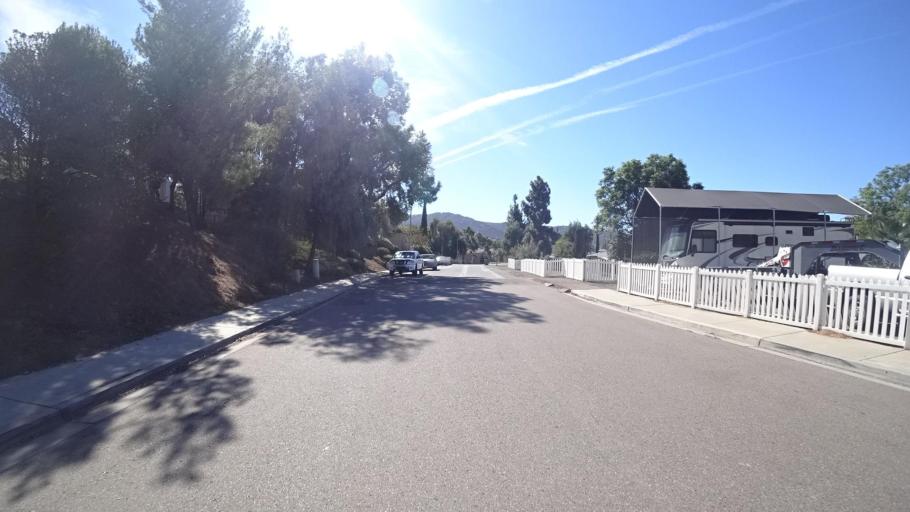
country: US
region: California
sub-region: San Diego County
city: Lakeside
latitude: 32.8443
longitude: -116.8882
